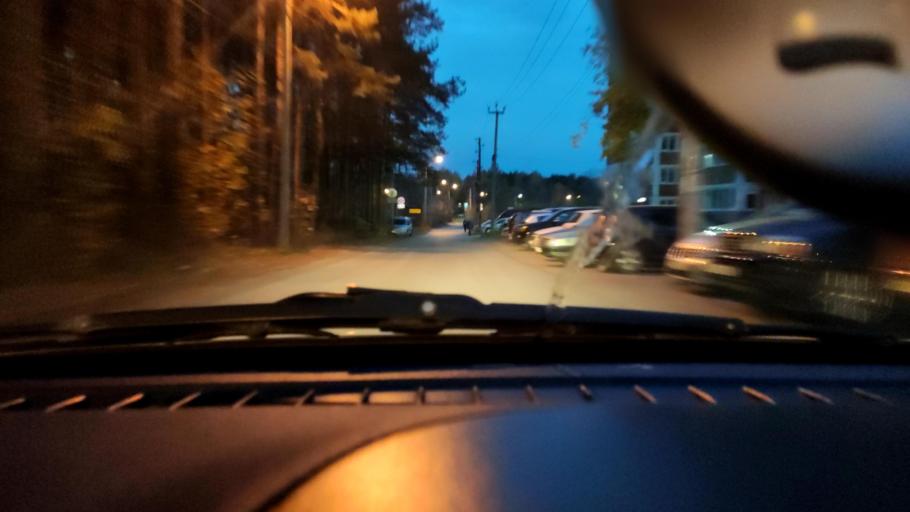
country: RU
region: Perm
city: Perm
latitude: 57.9955
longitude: 56.1815
